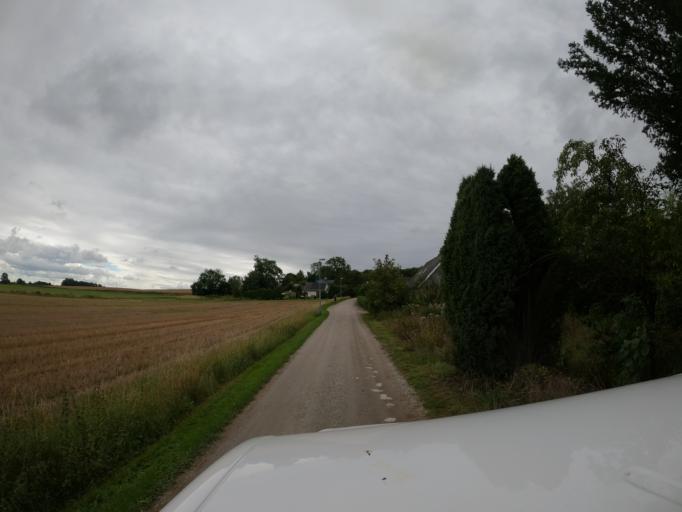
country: SE
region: Skane
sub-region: Lunds Kommun
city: Lund
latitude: 55.7809
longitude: 13.2144
